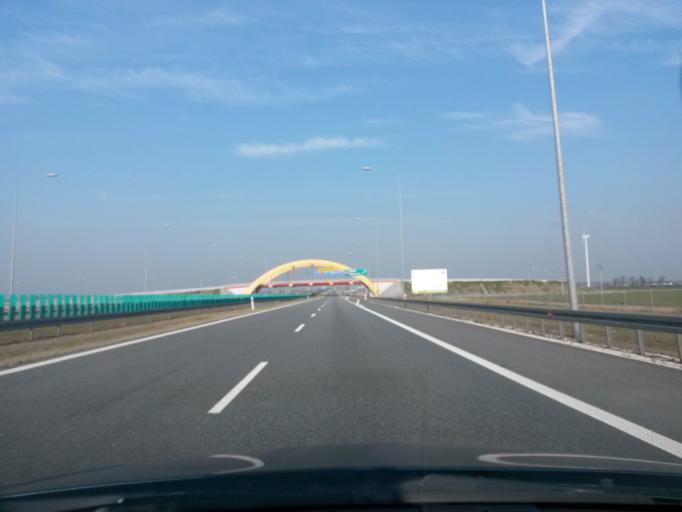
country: PL
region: Lodz Voivodeship
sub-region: Powiat kutnowski
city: Krzyzanow
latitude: 52.2229
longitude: 19.4681
